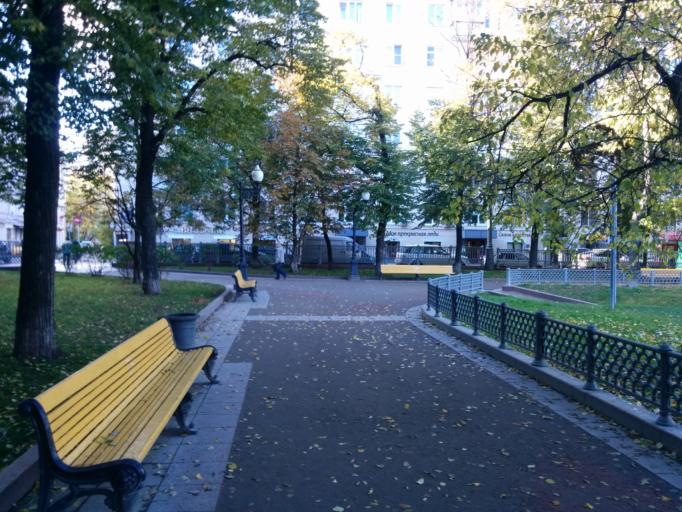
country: RU
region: Moscow
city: Moscow
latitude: 55.7631
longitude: 37.5925
